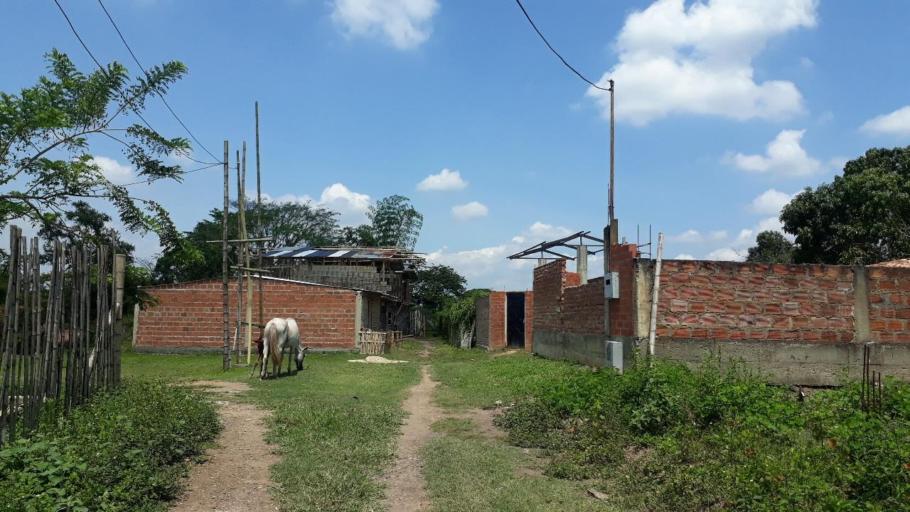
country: CO
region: Valle del Cauca
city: Jamundi
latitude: 3.1320
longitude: -76.5465
